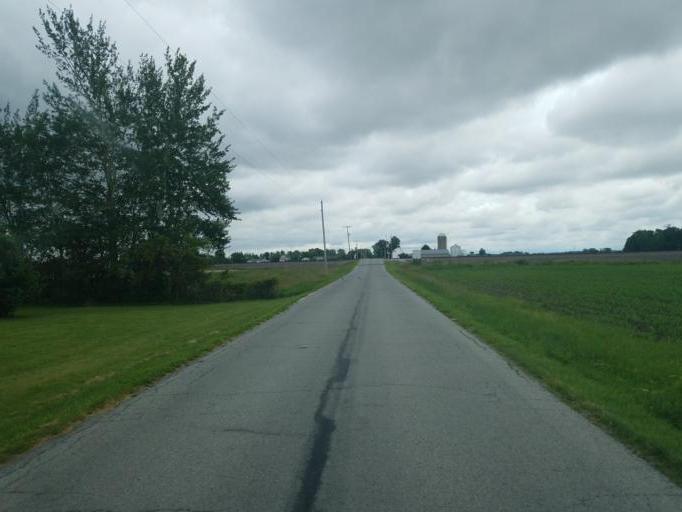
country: US
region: Ohio
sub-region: Crawford County
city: Bucyrus
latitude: 40.7757
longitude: -82.9894
